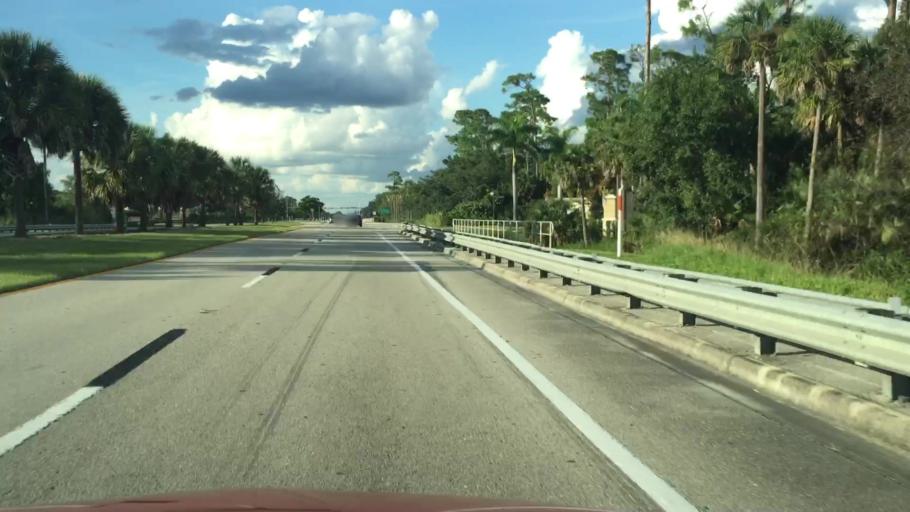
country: US
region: Florida
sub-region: Lee County
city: Estero
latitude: 26.4269
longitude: -81.7882
